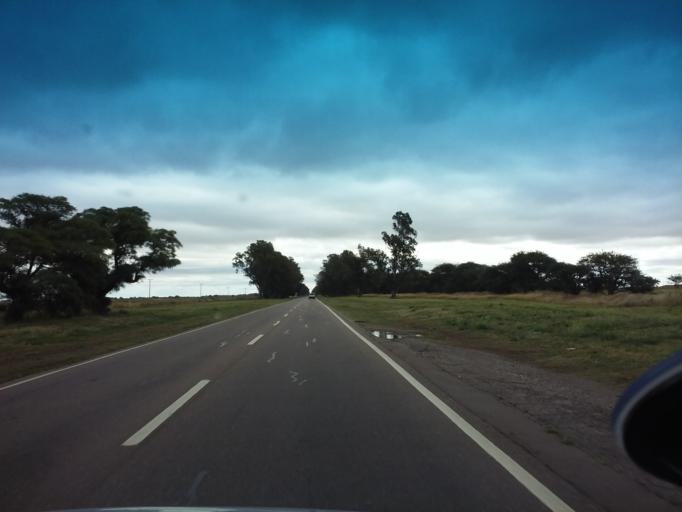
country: AR
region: La Pampa
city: Santa Rosa
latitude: -36.5719
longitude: -64.1490
